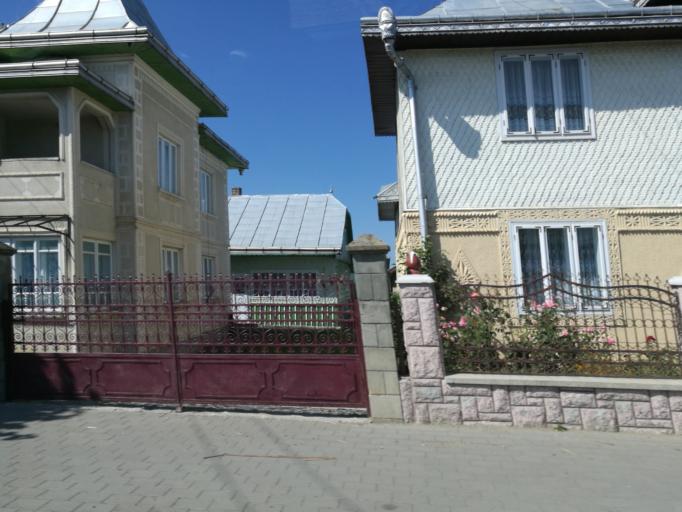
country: RO
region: Suceava
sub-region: Comuna Marginea
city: Marginea
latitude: 47.8072
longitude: 25.8164
